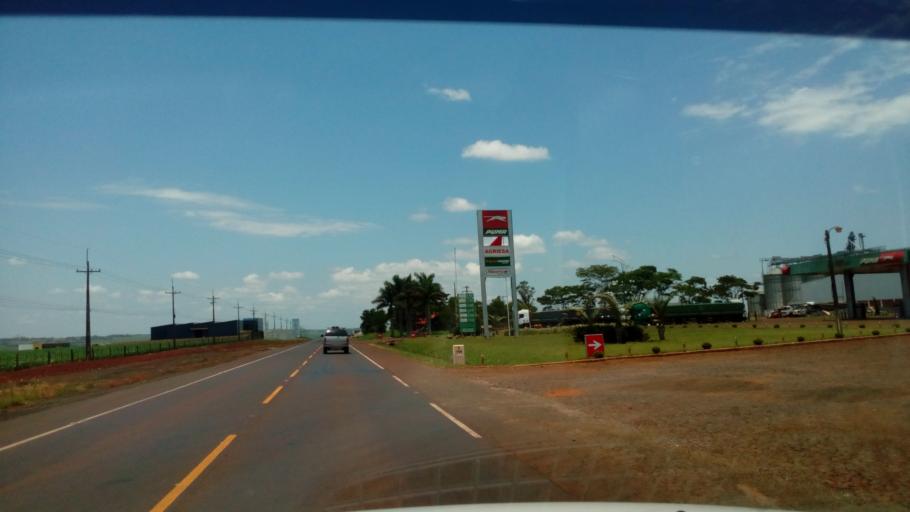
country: PY
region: Alto Parana
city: Naranjal
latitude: -25.8807
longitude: -55.1209
